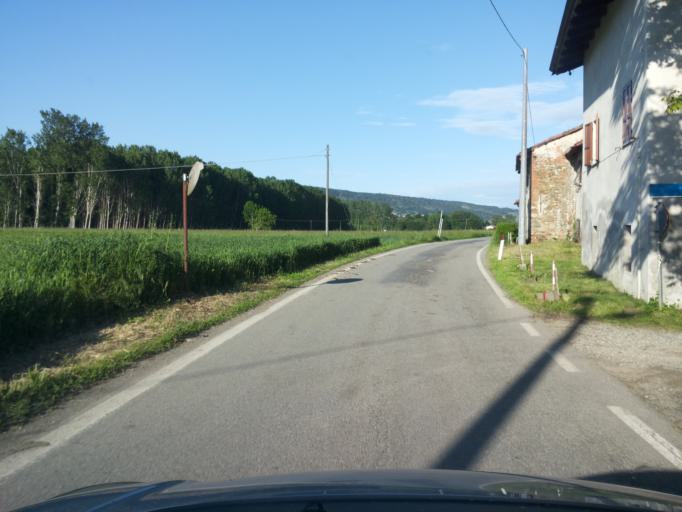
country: IT
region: Piedmont
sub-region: Provincia di Torino
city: Albiano d'Ivrea
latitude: 45.4417
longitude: 7.9553
